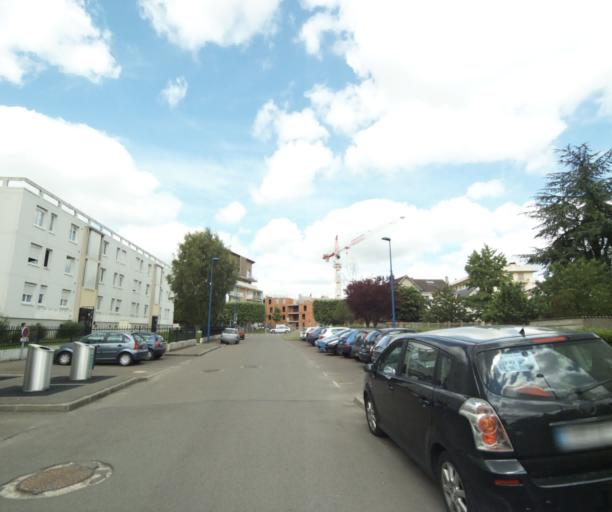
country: FR
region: Centre
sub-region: Departement d'Eure-et-Loir
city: Luisant
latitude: 48.4385
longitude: 1.4747
